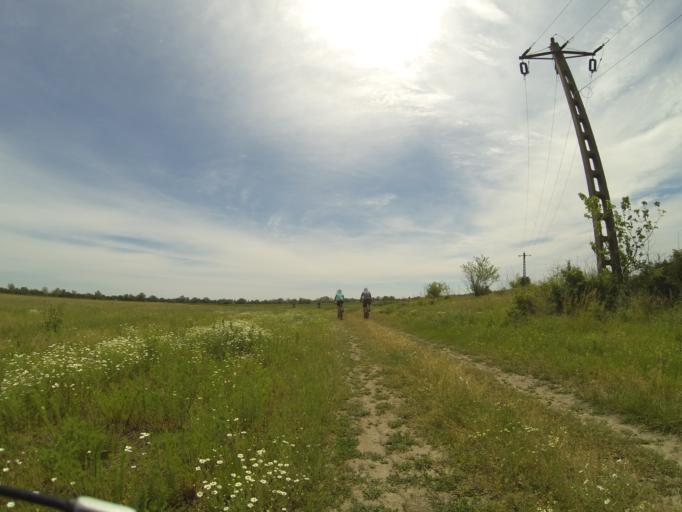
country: RO
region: Dolj
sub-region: Comuna Leu
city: Leu
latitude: 44.2012
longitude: 23.9757
